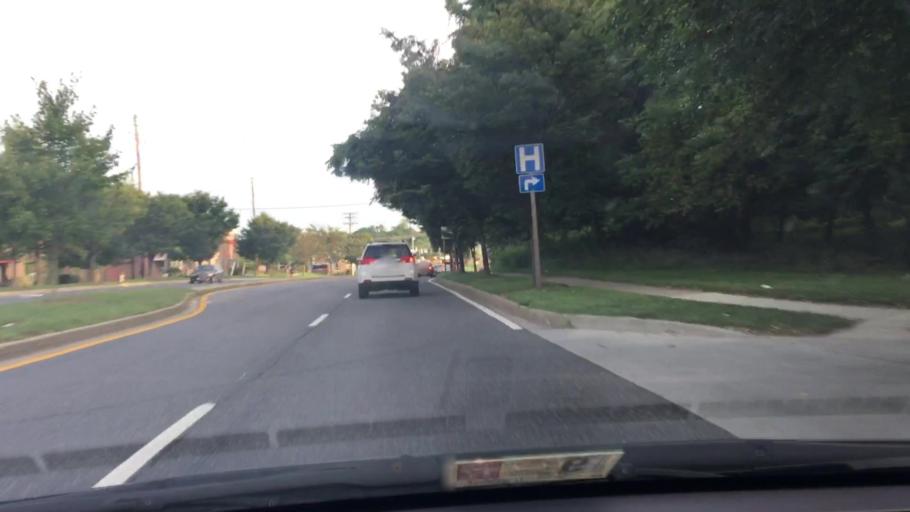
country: US
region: Maryland
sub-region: Montgomery County
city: Germantown
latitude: 39.1832
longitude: -77.2389
